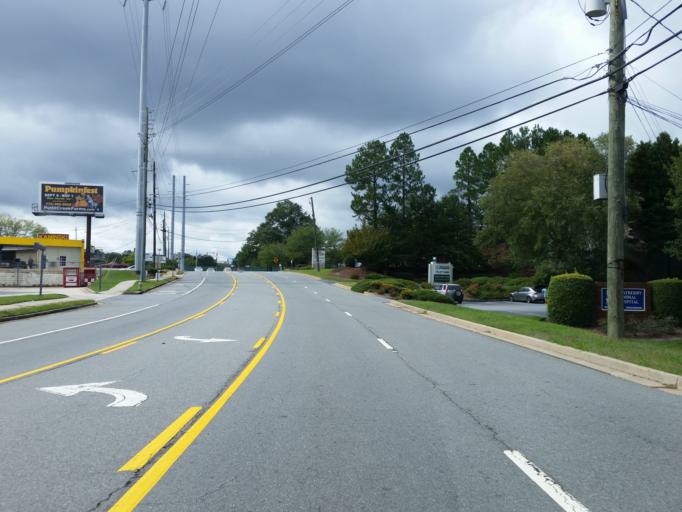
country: US
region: Georgia
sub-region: Cobb County
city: Marietta
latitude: 34.0173
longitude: -84.4891
